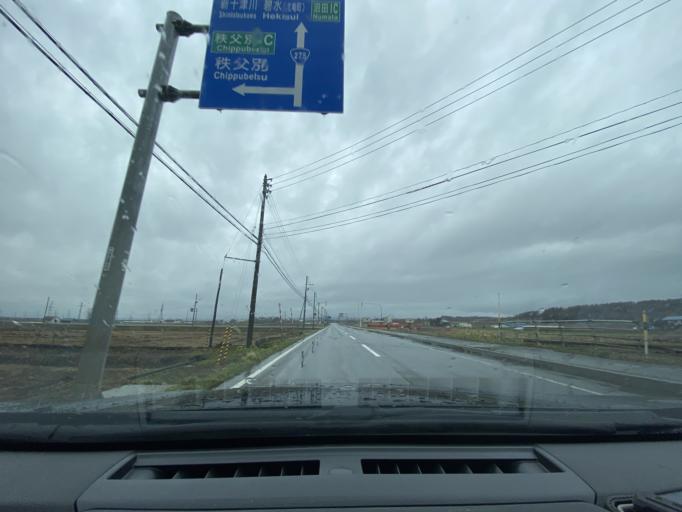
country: JP
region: Hokkaido
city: Fukagawa
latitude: 43.8137
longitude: 141.9652
